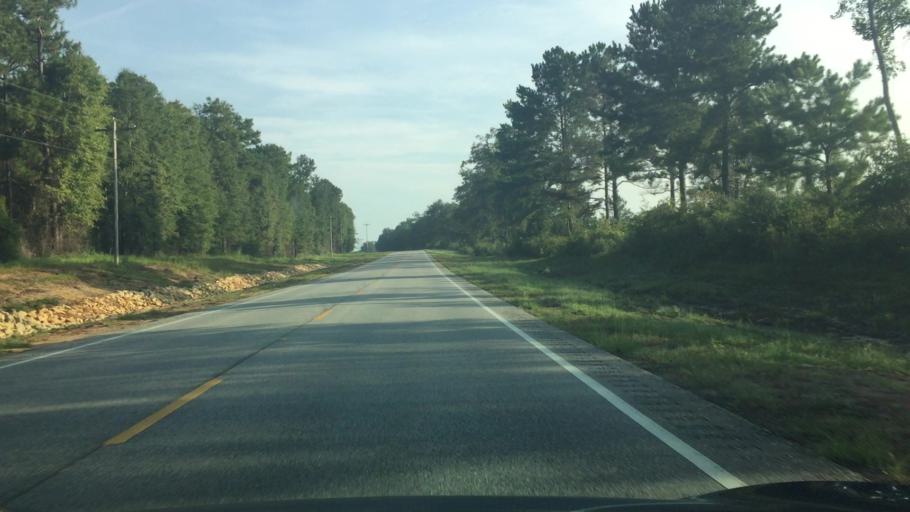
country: US
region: Alabama
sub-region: Covington County
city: Andalusia
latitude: 31.1568
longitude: -86.4585
